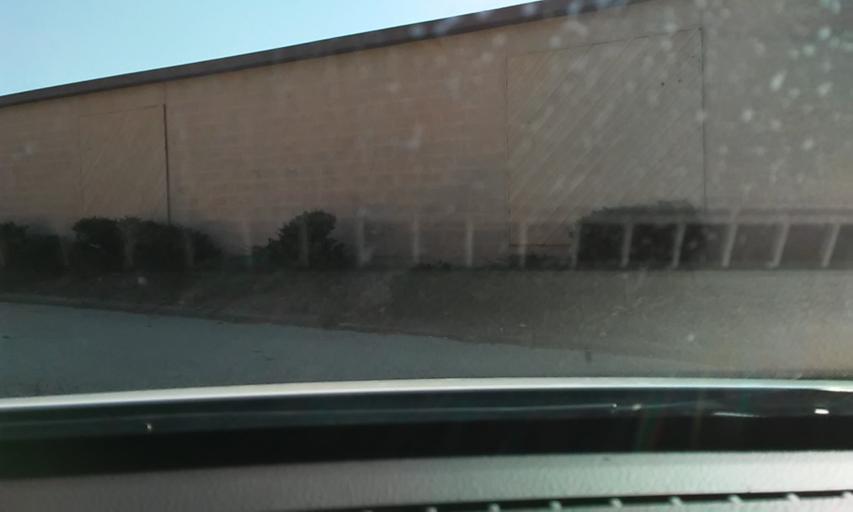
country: US
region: Wisconsin
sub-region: Waukesha County
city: Elm Grove
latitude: 43.0144
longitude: -88.0501
